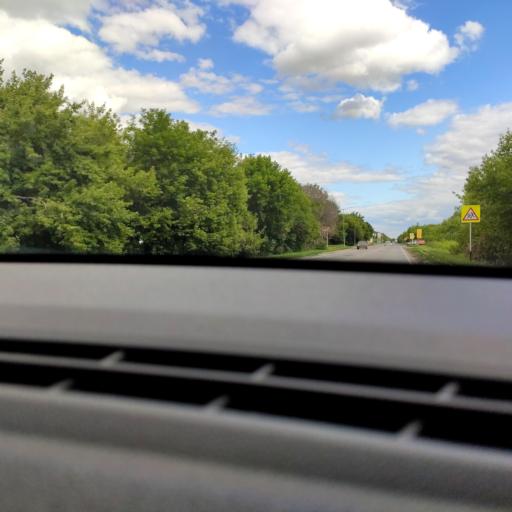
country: RU
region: Samara
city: Podstepki
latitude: 53.5734
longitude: 49.0814
